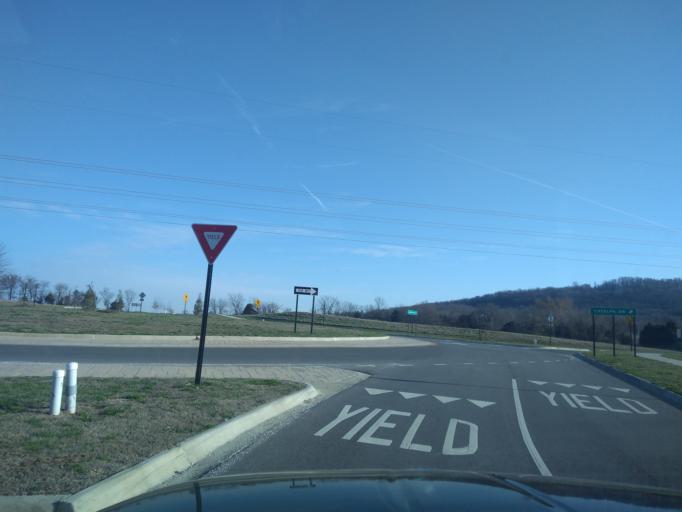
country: US
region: Arkansas
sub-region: Washington County
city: Farmington
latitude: 36.0509
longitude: -94.2199
